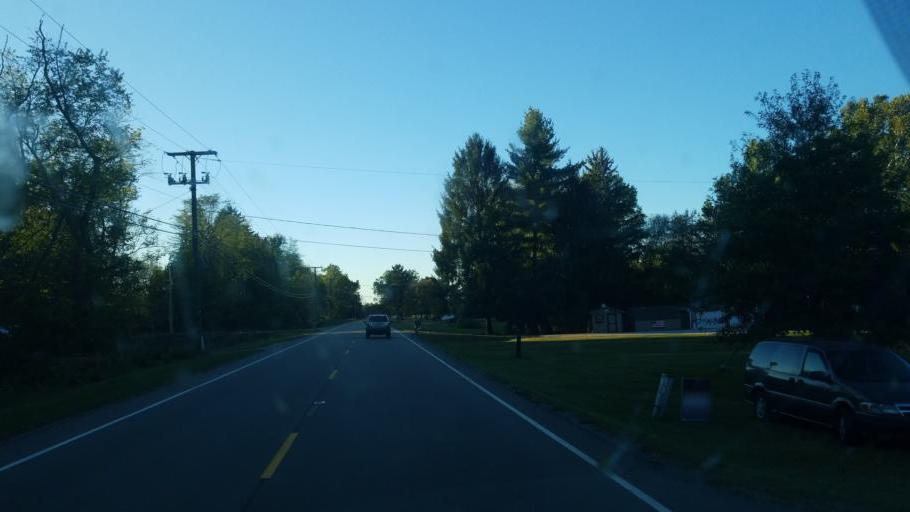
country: US
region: Ohio
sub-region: Coshocton County
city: Coshocton
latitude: 40.3127
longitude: -81.9325
